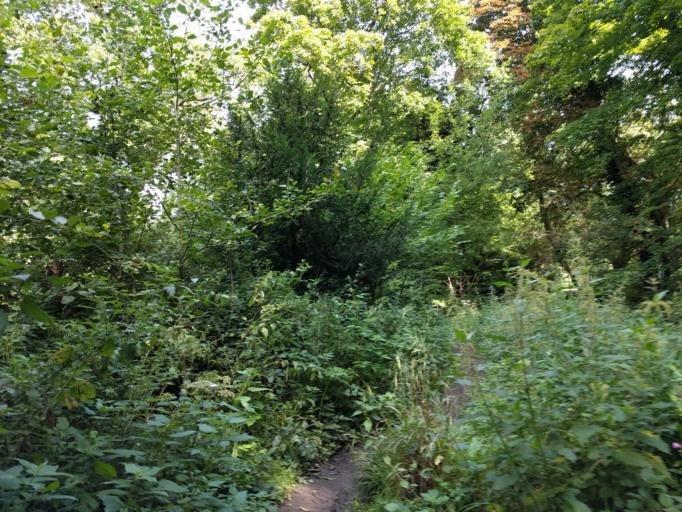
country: GB
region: England
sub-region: Surrey
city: Chilworth
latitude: 51.2185
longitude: -0.5226
